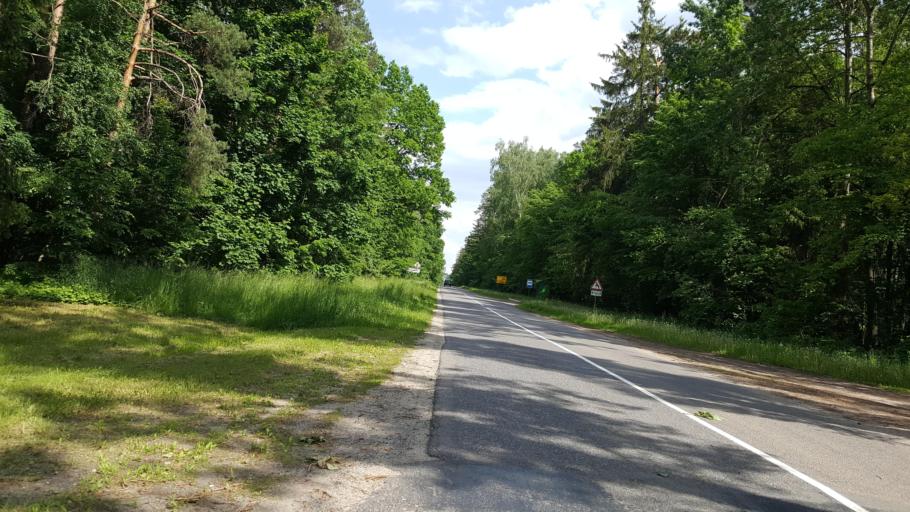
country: PL
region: Podlasie
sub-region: Powiat hajnowski
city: Bialowieza
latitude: 52.6047
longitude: 24.1092
